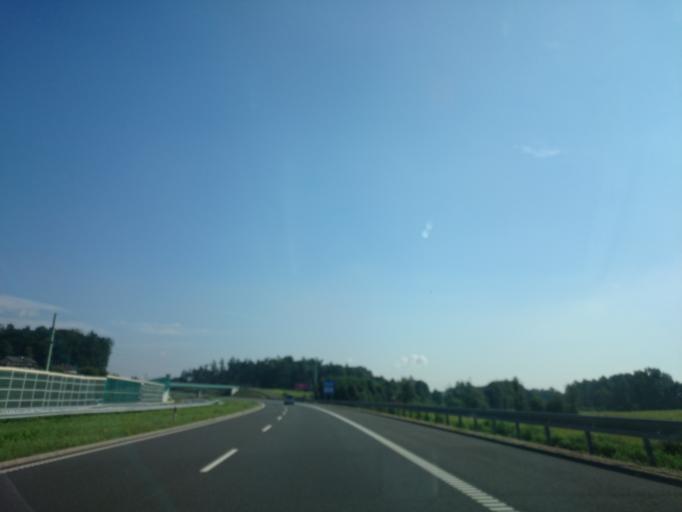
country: PL
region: Silesian Voivodeship
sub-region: Powiat rybnicki
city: Swierklany Gorne
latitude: 50.0498
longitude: 18.6415
